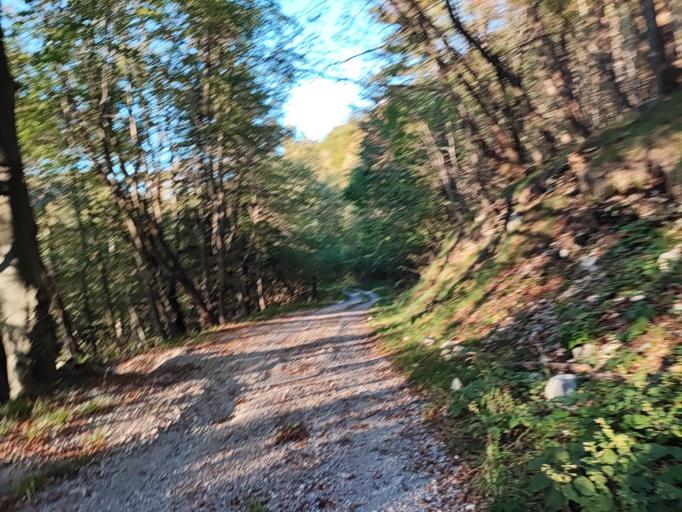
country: SI
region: Nova Gorica
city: Sempas
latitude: 46.0244
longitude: 13.7798
